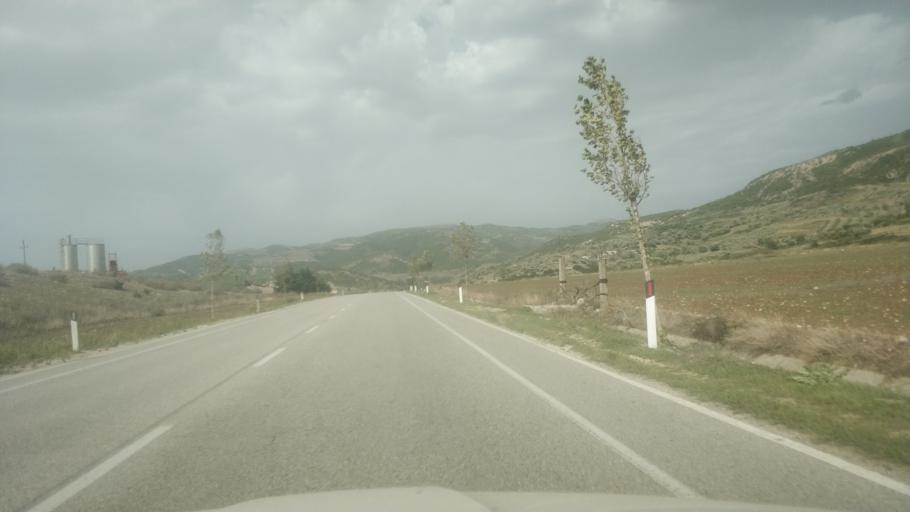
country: AL
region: Gjirokaster
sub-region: Rrethi i Tepelenes
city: Memaliaj
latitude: 40.3691
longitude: 19.9081
